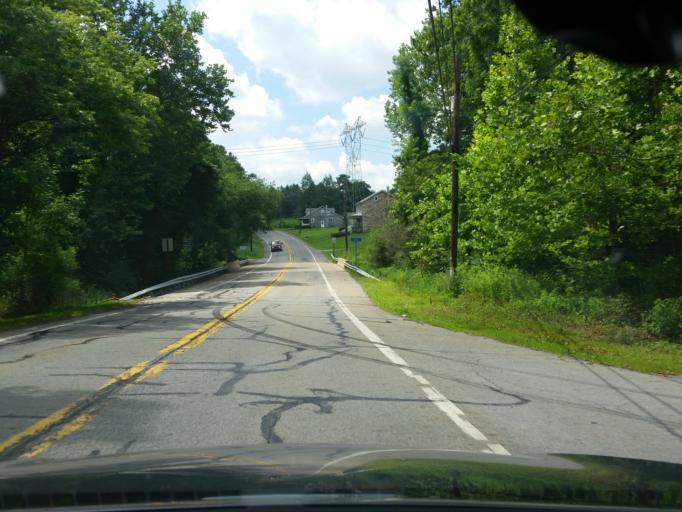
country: US
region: Pennsylvania
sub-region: Dauphin County
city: Matamoras
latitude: 40.4268
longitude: -76.9384
